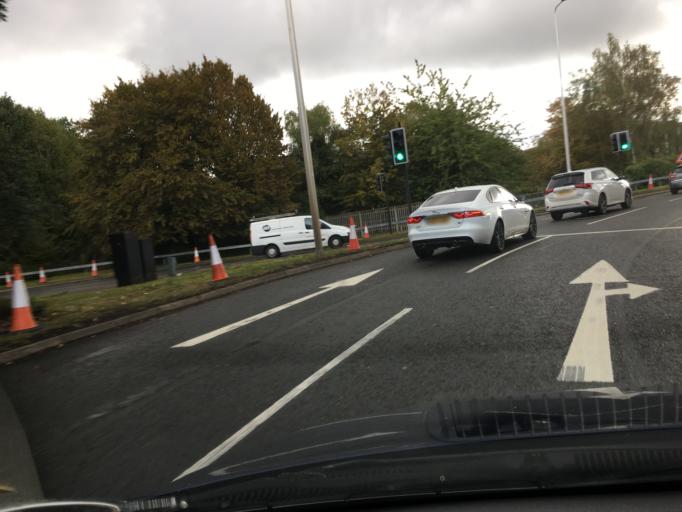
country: GB
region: England
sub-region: Bracknell Forest
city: Bracknell
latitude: 51.4134
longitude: -0.7607
